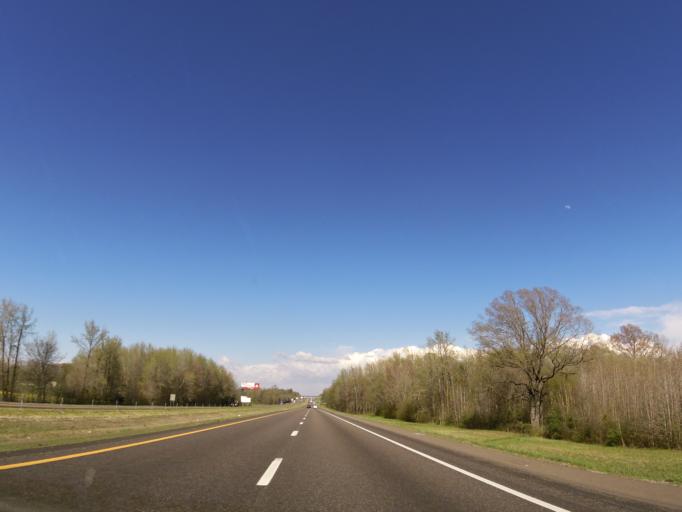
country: US
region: Tennessee
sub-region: Decatur County
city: Parsons
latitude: 35.8445
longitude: -88.0773
